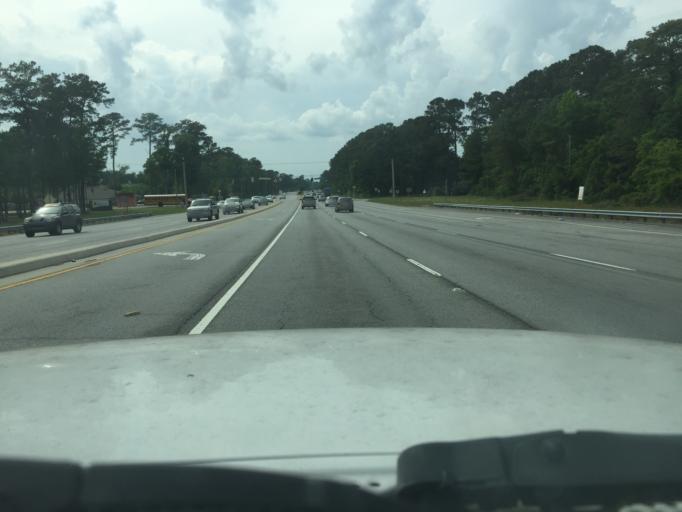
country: US
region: Georgia
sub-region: Chatham County
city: Whitemarsh Island
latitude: 32.0364
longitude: -80.9889
